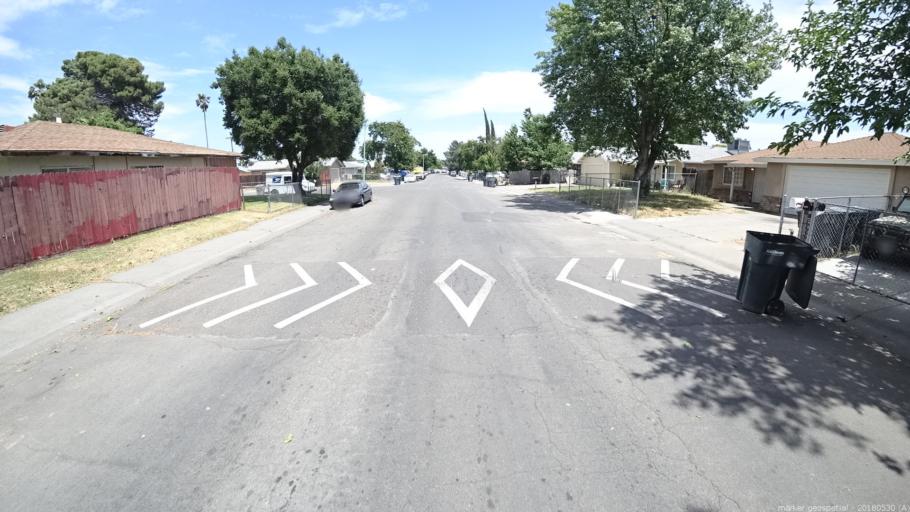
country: US
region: California
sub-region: Sacramento County
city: Sacramento
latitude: 38.6236
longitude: -121.4633
